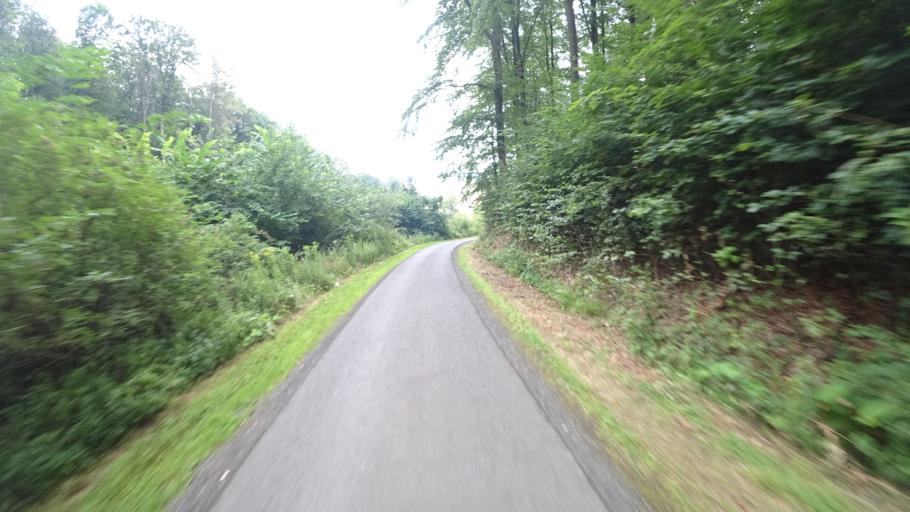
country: DE
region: Rheinland-Pfalz
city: Hohr-Grenzhausen
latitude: 50.4196
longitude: 7.6646
